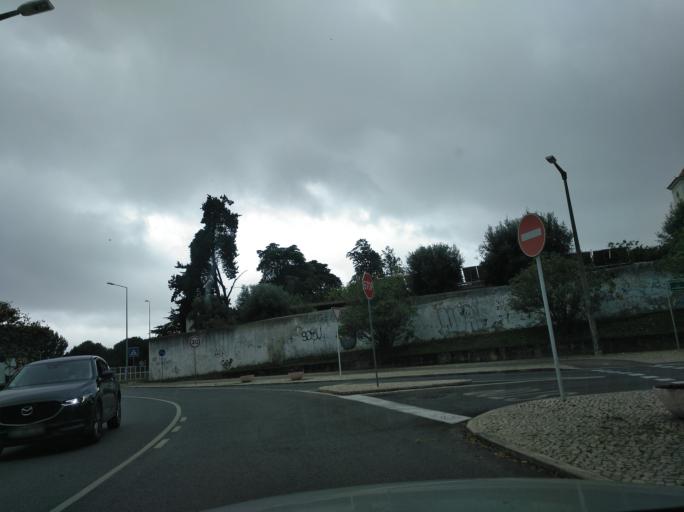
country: PT
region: Lisbon
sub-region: Loures
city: Moscavide
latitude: 38.7809
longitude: -9.1066
